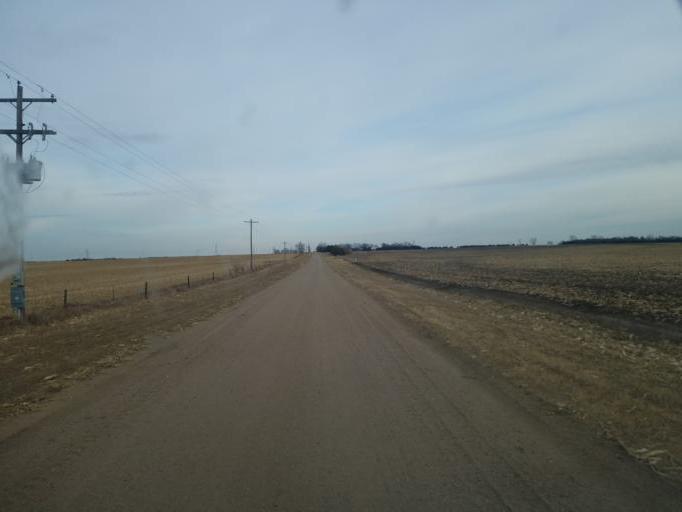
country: US
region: Nebraska
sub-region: Holt County
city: O'Neill
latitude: 42.4368
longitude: -98.3346
